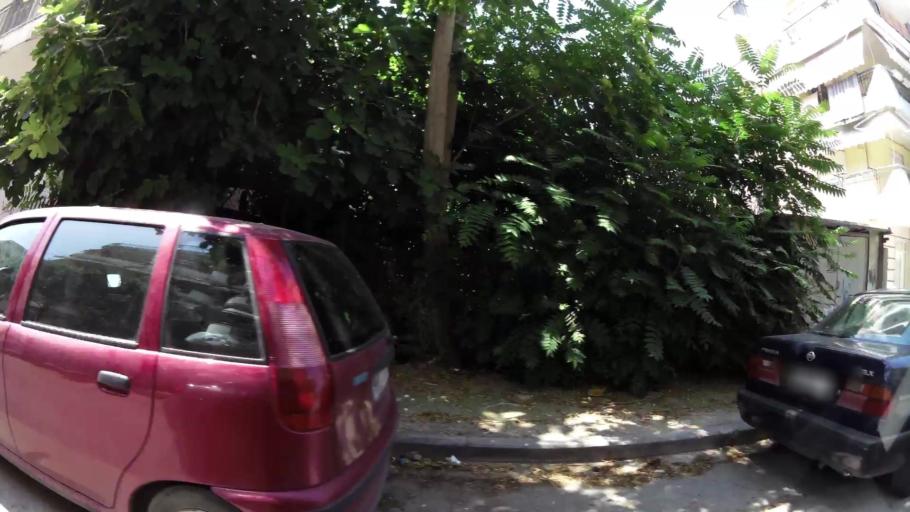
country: GR
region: Central Macedonia
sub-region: Nomos Thessalonikis
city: Evosmos
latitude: 40.6711
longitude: 22.9038
